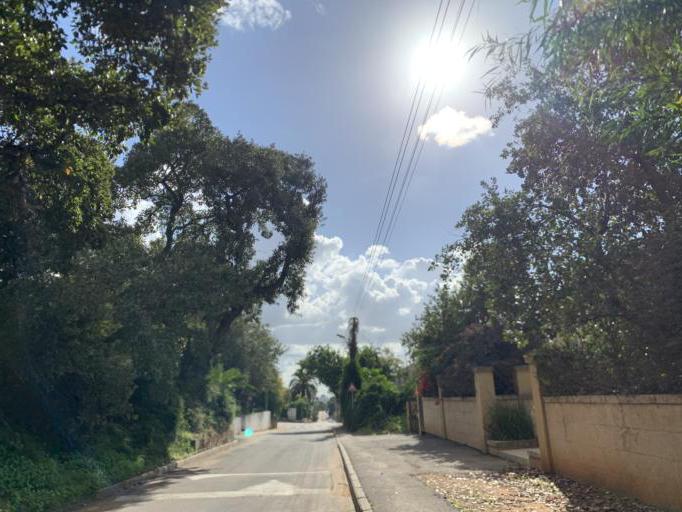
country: IL
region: Central District
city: Hod HaSharon
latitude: 32.1683
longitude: 34.8897
